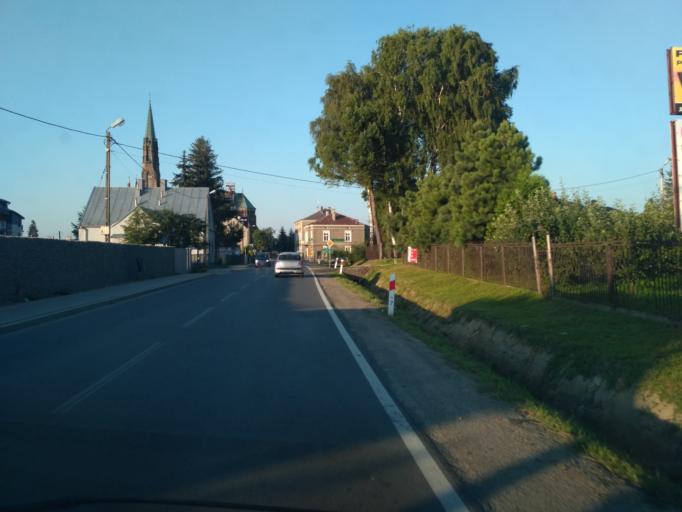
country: PL
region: Subcarpathian Voivodeship
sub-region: Powiat krosnienski
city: Korczyna
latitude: 49.7171
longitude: 21.8104
